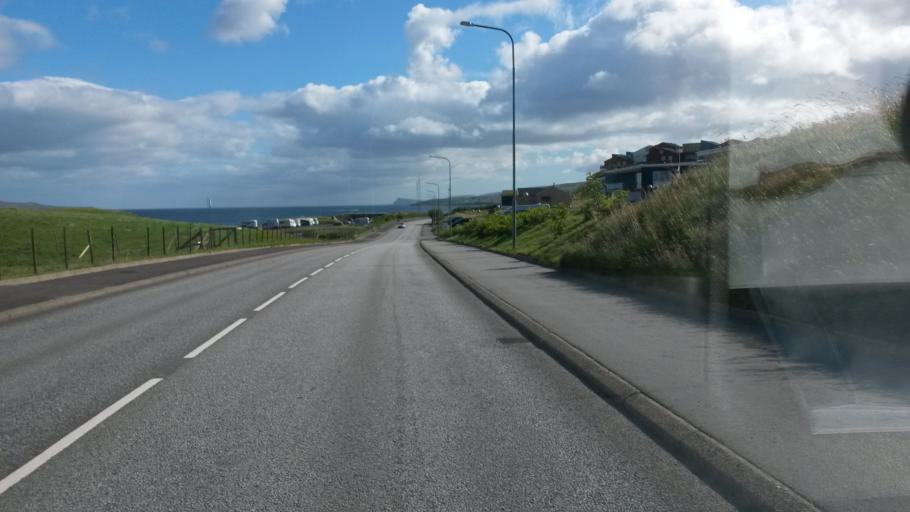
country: FO
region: Streymoy
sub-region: Torshavn
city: Torshavn
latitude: 62.0191
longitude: -6.7568
